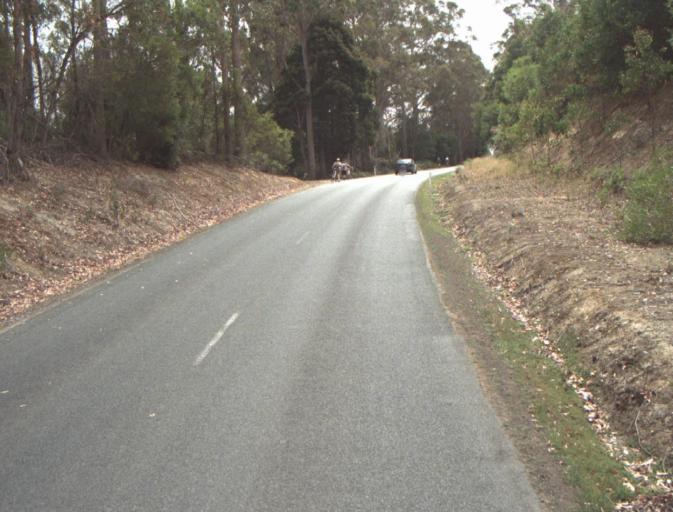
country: AU
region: Tasmania
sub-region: Launceston
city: Mayfield
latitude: -41.2129
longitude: 147.2122
